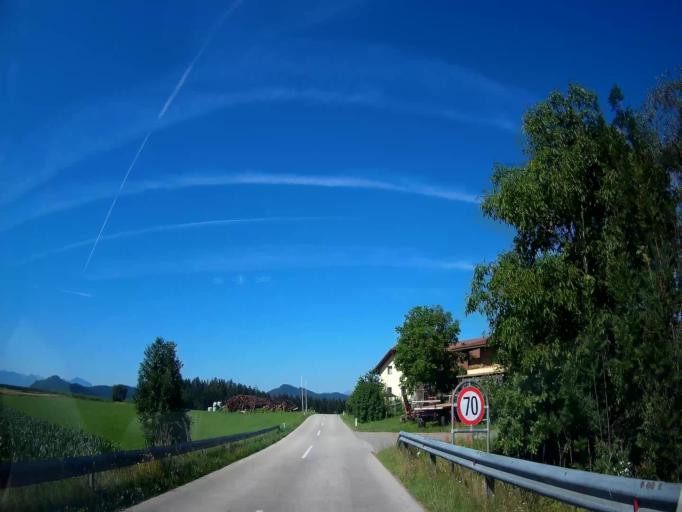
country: AT
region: Carinthia
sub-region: Politischer Bezirk Klagenfurt Land
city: Maria Saal
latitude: 46.6950
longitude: 14.3871
